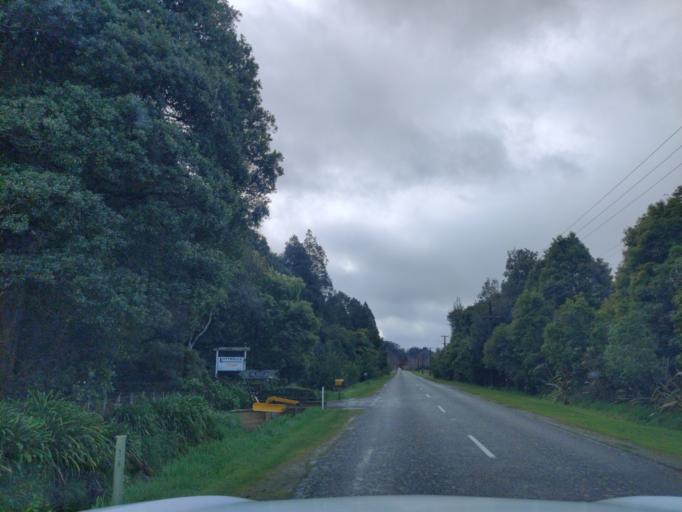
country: NZ
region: Manawatu-Wanganui
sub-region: Palmerston North City
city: Palmerston North
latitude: -40.1764
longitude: 175.7911
